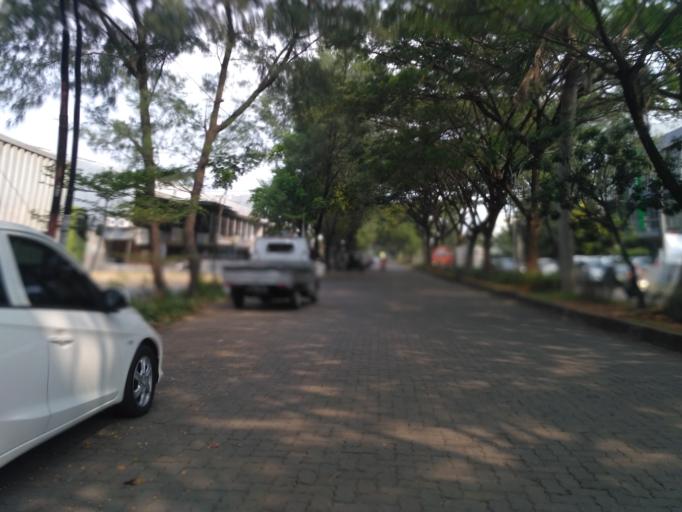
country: ID
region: Central Java
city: Semarang
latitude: -6.9636
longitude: 110.3907
